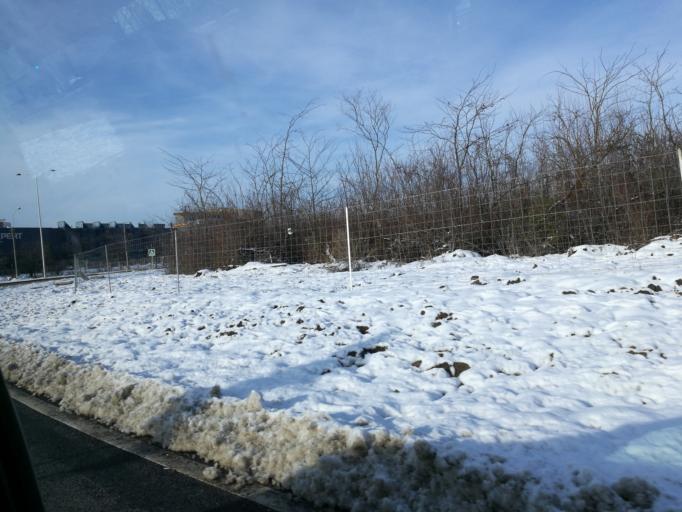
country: RO
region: Ilfov
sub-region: Comuna Fundeni-Dobroesti
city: Fundeni
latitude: 44.4789
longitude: 26.1265
